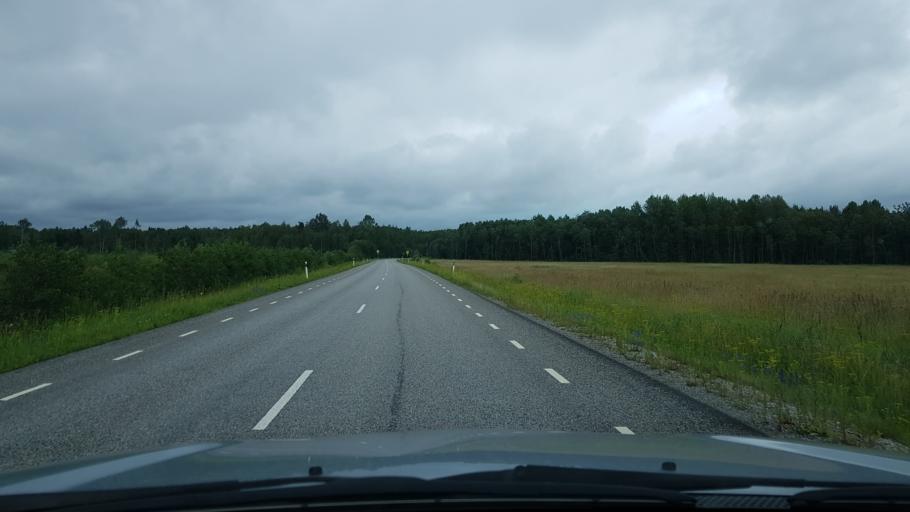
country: EE
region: Ida-Virumaa
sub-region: Narva-Joesuu linn
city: Narva-Joesuu
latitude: 59.3676
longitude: 27.9294
